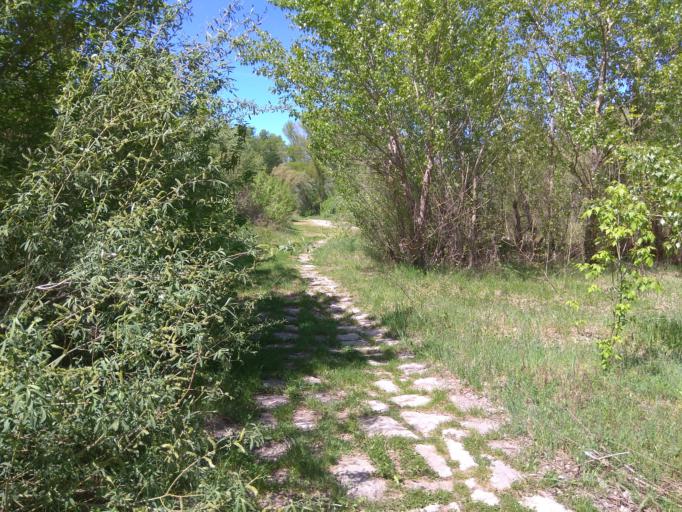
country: HU
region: Gyor-Moson-Sopron
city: Gyor
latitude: 47.7937
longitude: 17.6603
